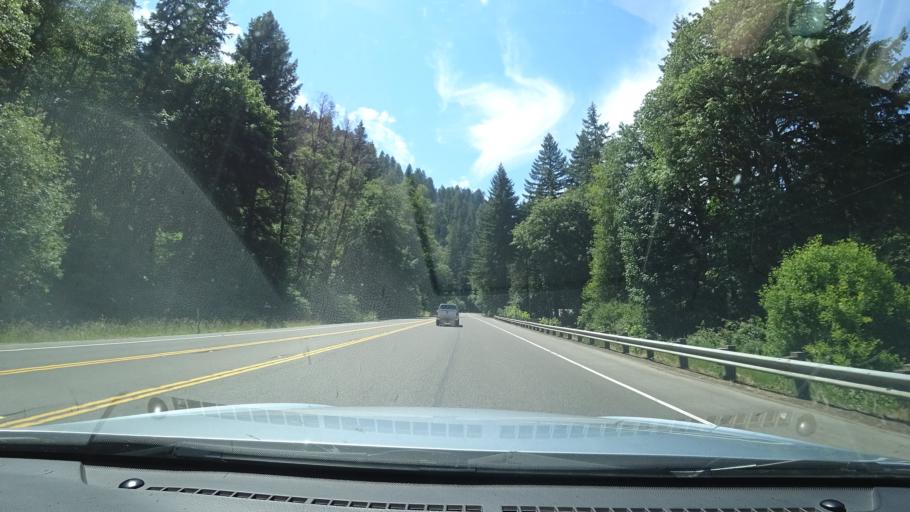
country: US
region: Oregon
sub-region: Lane County
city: Veneta
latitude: 43.9988
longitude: -123.6920
